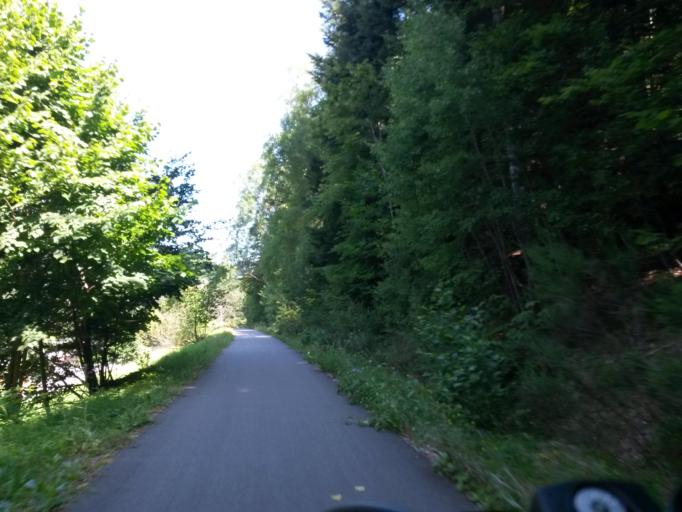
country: DE
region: Baden-Wuerttemberg
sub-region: Karlsruhe Region
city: Bad Wildbad
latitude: 48.7314
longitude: 8.5440
